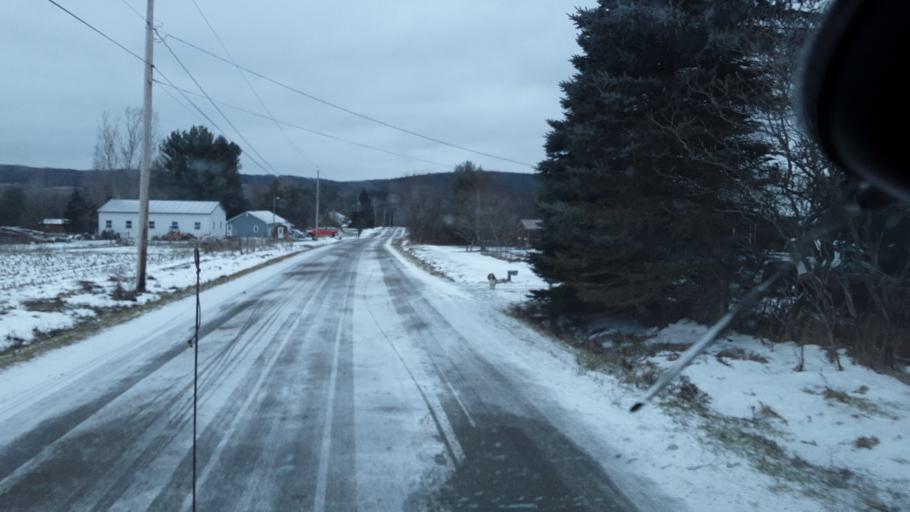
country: US
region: New York
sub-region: Allegany County
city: Friendship
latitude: 42.2950
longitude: -78.1624
